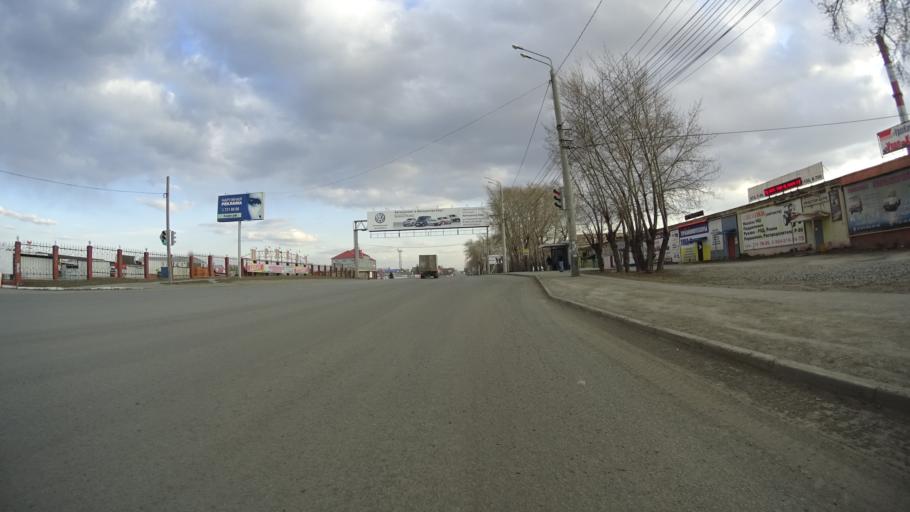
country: RU
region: Chelyabinsk
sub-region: Gorod Chelyabinsk
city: Chelyabinsk
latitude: 55.1108
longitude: 61.3867
